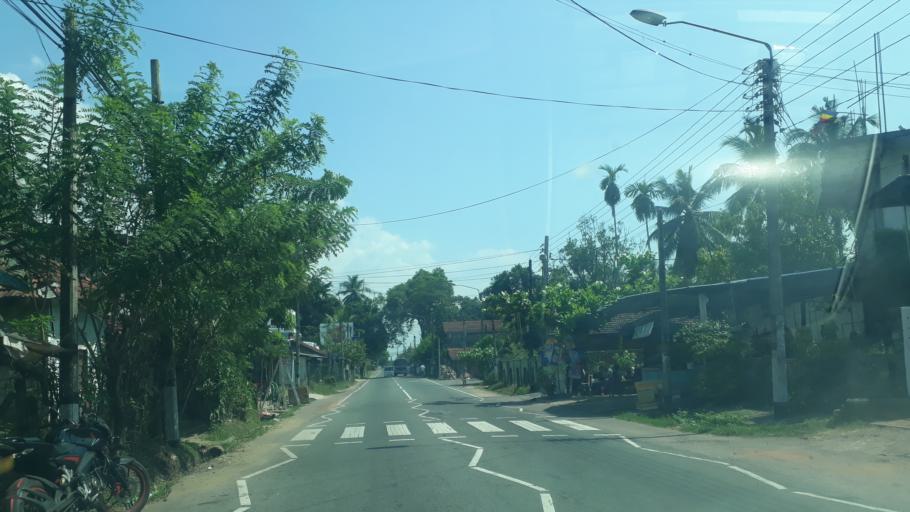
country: LK
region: Western
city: Gampaha
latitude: 7.0818
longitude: 80.0113
